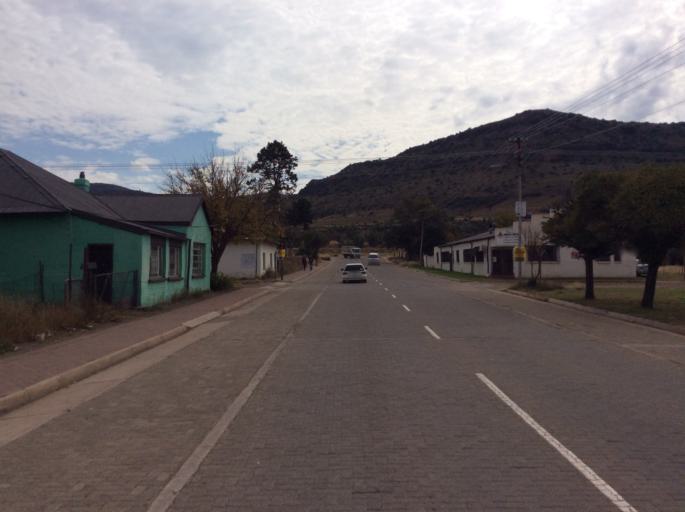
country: LS
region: Mafeteng
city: Mafeteng
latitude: -29.7258
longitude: 27.0389
